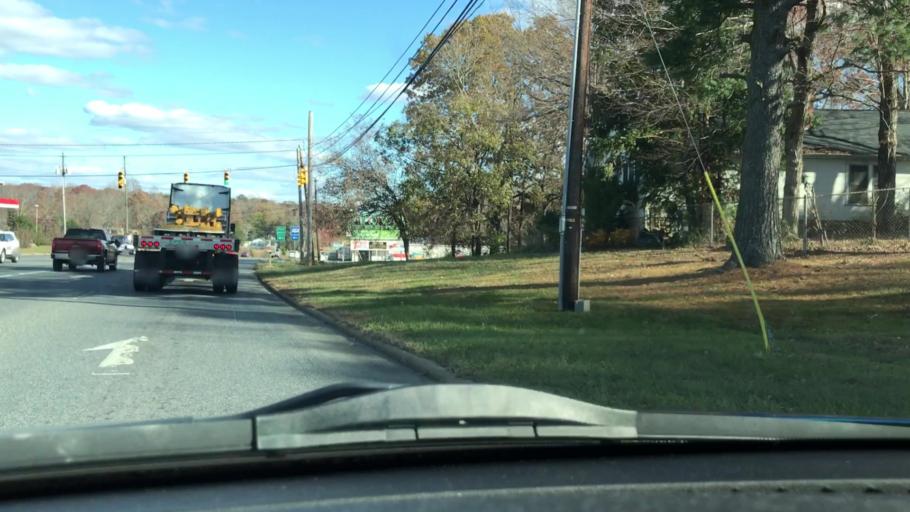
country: US
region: North Carolina
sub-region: Randolph County
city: Franklinville
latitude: 35.7252
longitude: -79.7409
